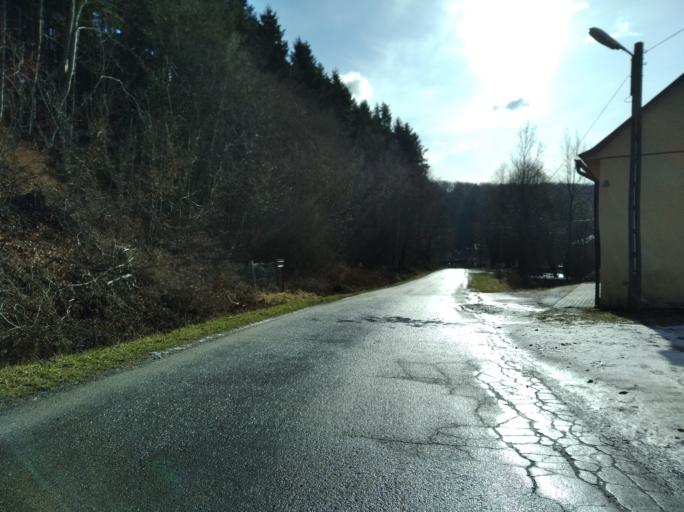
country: PL
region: Subcarpathian Voivodeship
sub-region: Powiat strzyzowski
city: Strzyzow
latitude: 49.8947
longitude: 21.7771
